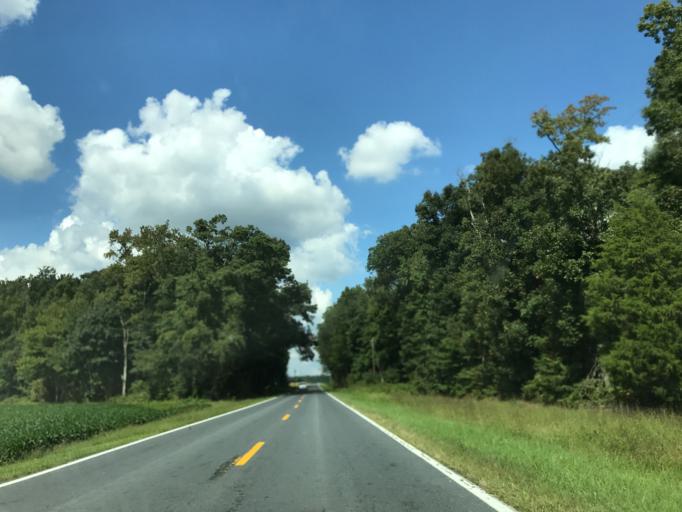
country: US
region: Maryland
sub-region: Caroline County
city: Ridgely
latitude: 39.0385
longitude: -75.9091
